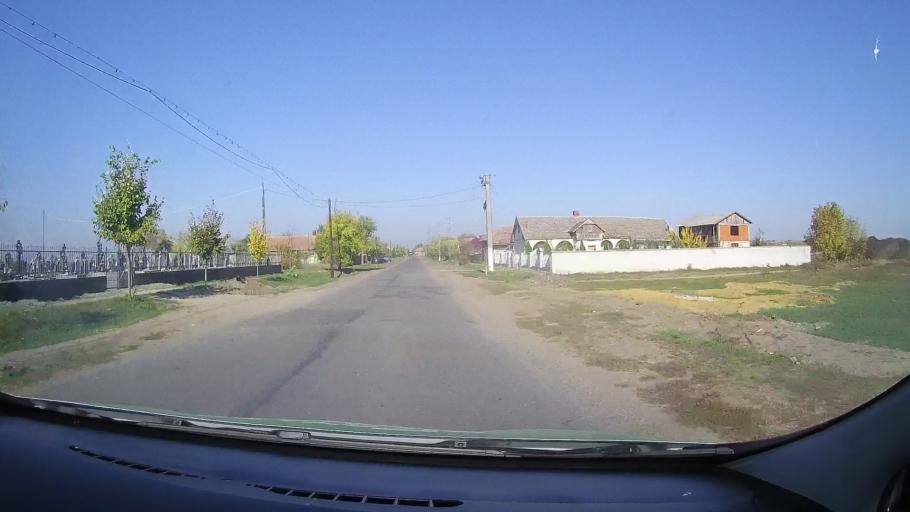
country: RO
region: Satu Mare
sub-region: Comuna Ciumesti
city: Ciumesti
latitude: 47.6531
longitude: 22.3356
